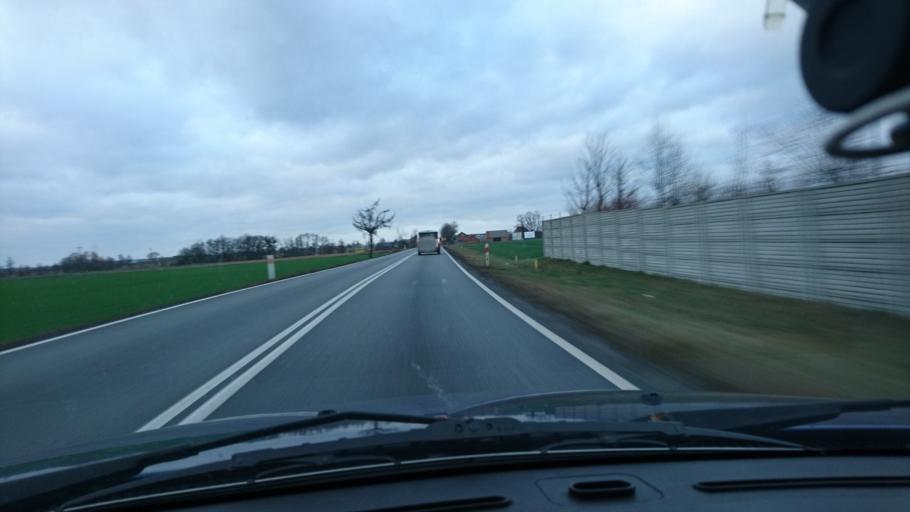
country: PL
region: Opole Voivodeship
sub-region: Powiat kluczborski
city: Kluczbork
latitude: 51.0025
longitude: 18.2051
